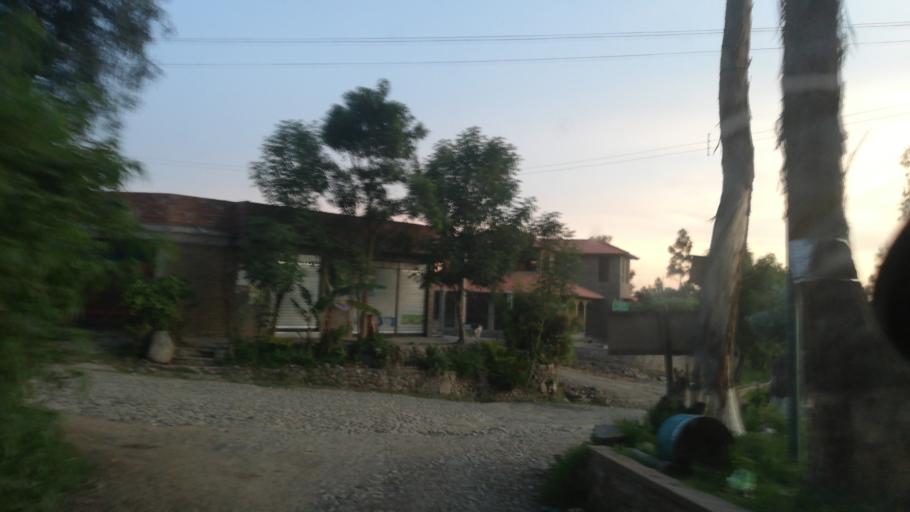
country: BO
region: Cochabamba
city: Cochabamba
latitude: -17.3210
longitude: -66.2090
